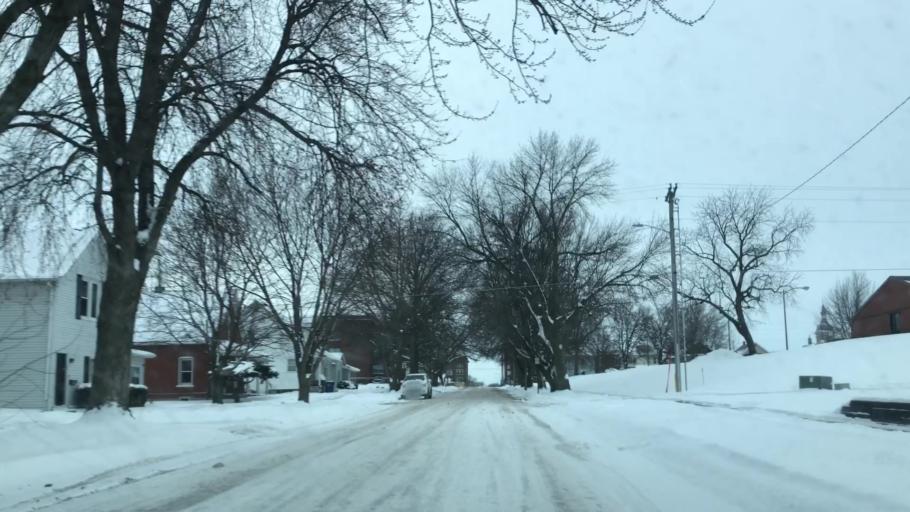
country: US
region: Iowa
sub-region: Marshall County
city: Marshalltown
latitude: 42.0532
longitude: -92.9097
